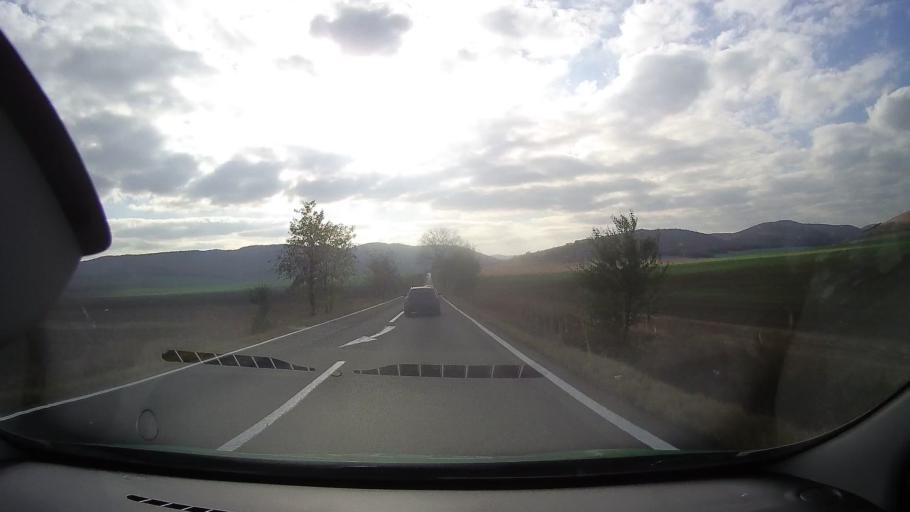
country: RO
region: Tulcea
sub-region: Comuna Nalbant
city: Nicolae Balcescu
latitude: 44.9788
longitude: 28.5474
